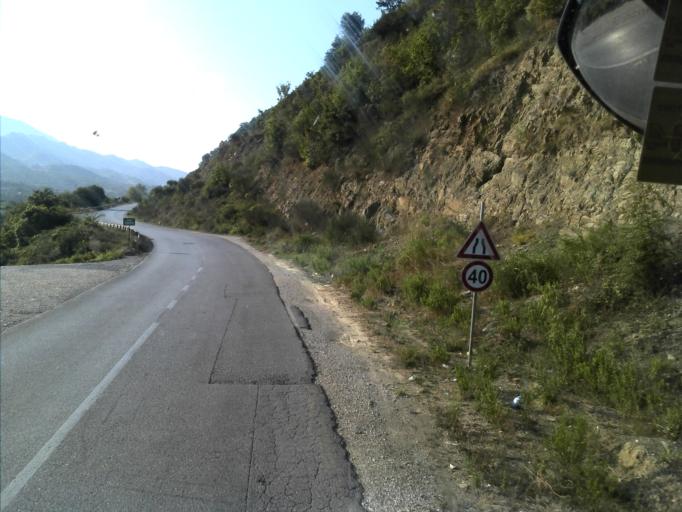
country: AL
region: Gjirokaster
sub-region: Rrethi i Gjirokastres
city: Picar
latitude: 40.2339
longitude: 20.0802
